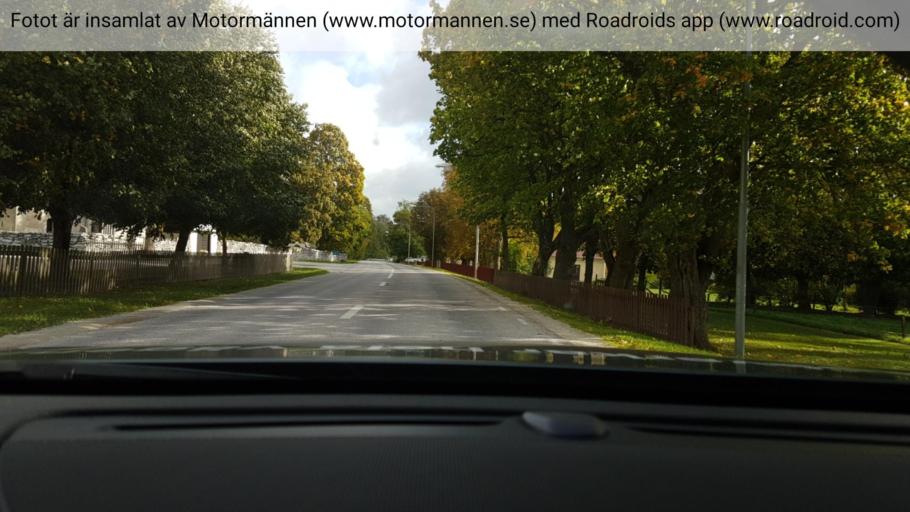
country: SE
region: Gotland
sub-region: Gotland
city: Visby
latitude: 57.6693
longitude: 18.4735
